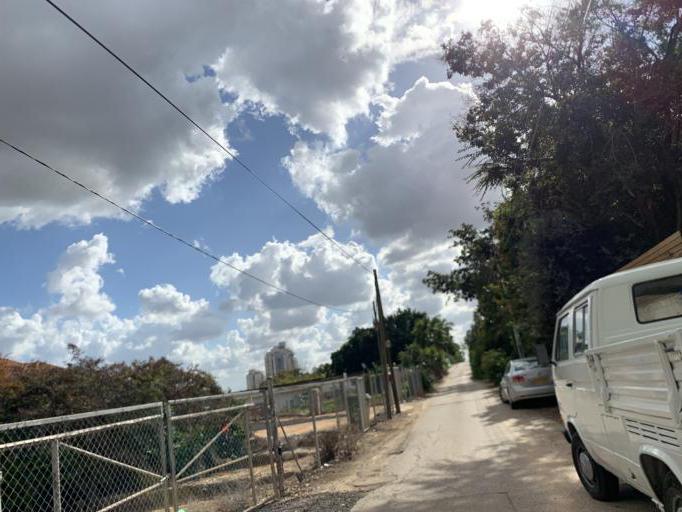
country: IL
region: Central District
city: Hod HaSharon
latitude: 32.1696
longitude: 34.8913
